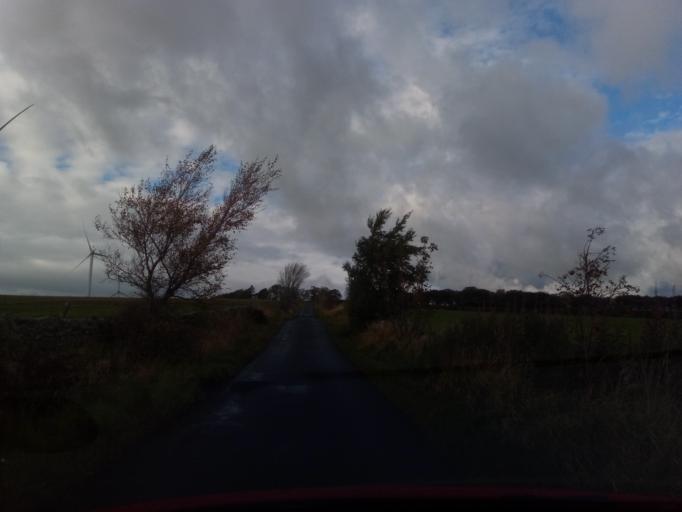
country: GB
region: Scotland
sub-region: The Scottish Borders
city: Galashiels
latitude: 55.6830
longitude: -2.8443
